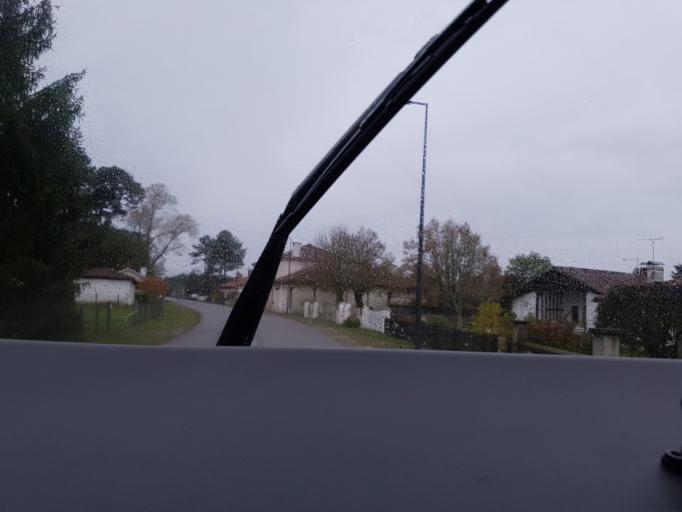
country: FR
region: Aquitaine
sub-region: Departement de la Gironde
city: Saint-Symphorien
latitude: 44.2620
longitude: -0.5210
